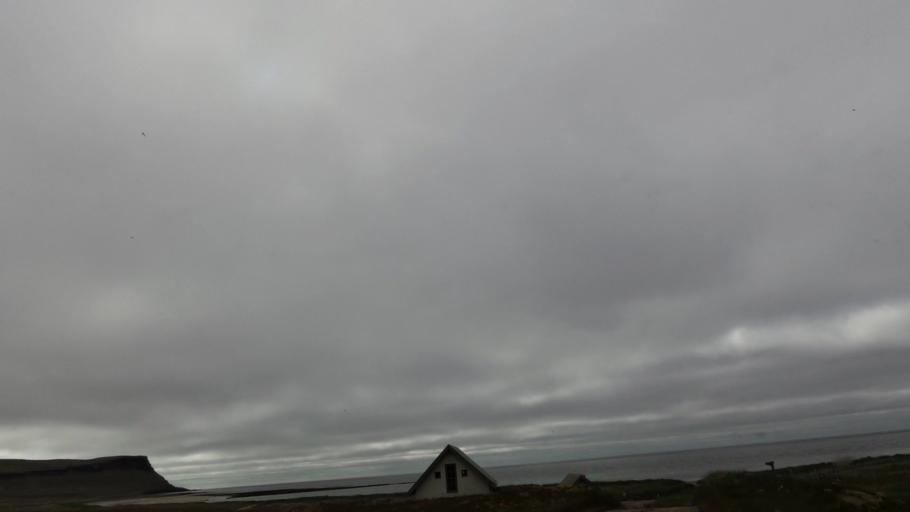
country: IS
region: West
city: Olafsvik
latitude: 65.5281
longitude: -24.4564
